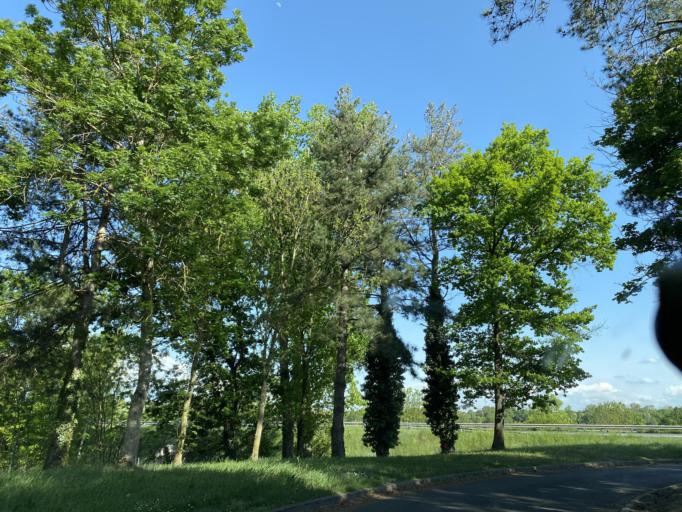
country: FR
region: Auvergne
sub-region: Departement du Puy-de-Dome
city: Culhat
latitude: 45.8358
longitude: 3.2986
